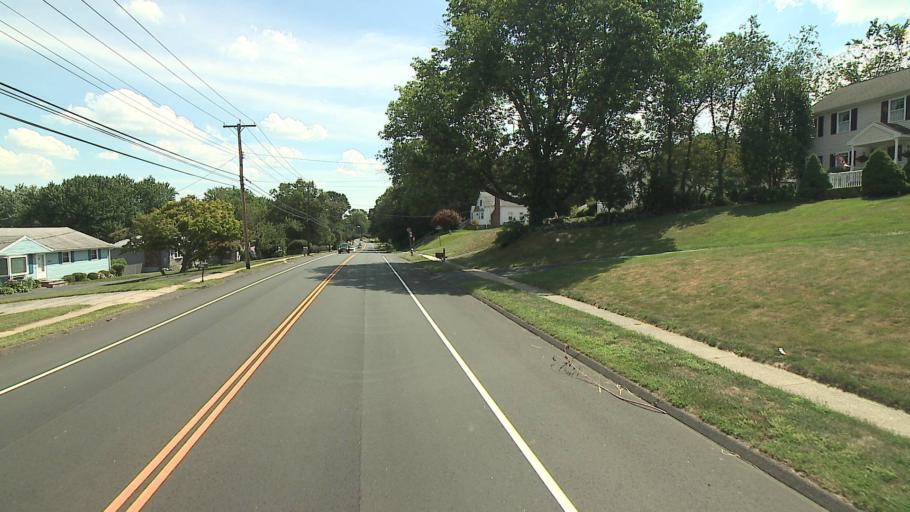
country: US
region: Connecticut
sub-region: Fairfield County
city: Stratford
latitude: 41.2231
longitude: -73.1506
